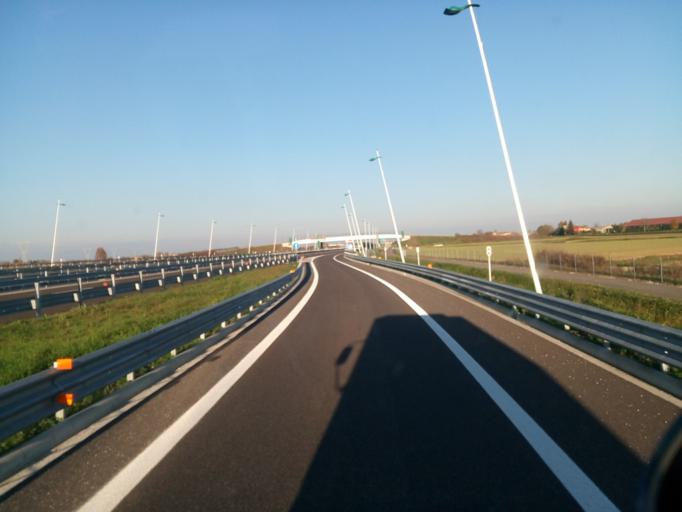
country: IT
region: Veneto
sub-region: Provincia di Padova
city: Bastia
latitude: 45.3913
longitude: 11.6183
